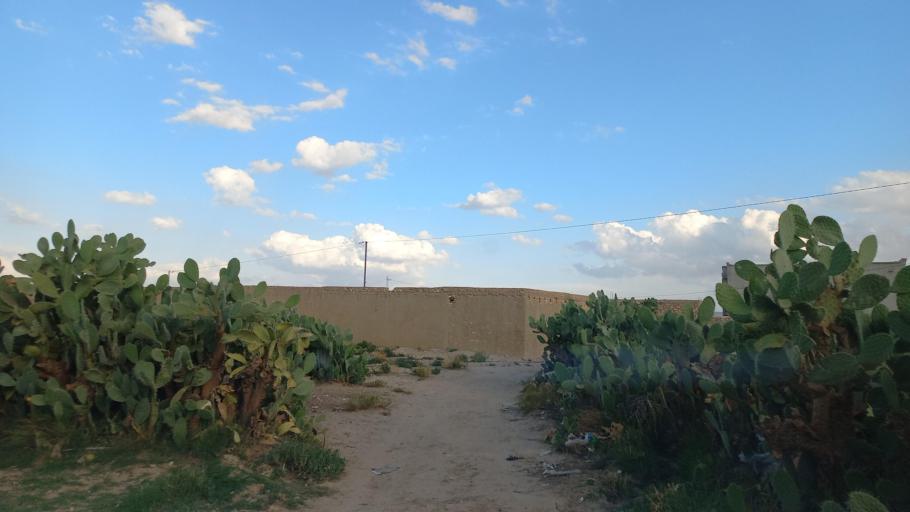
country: TN
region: Al Qasrayn
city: Sbiba
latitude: 35.3861
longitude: 9.0476
